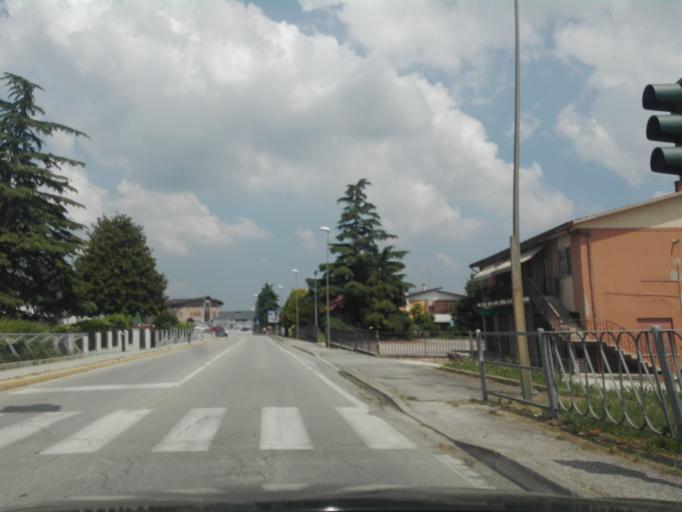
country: IT
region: Veneto
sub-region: Provincia di Rovigo
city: Adria
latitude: 45.0535
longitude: 12.0639
